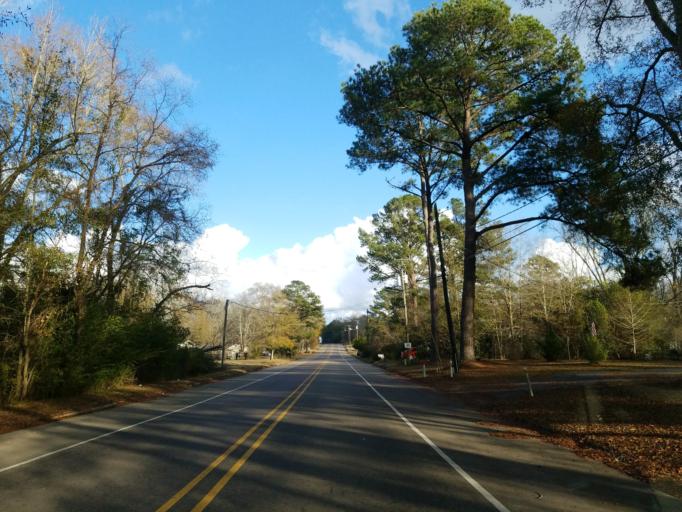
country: US
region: Mississippi
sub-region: Jones County
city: Sharon
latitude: 31.7881
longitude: -89.0461
